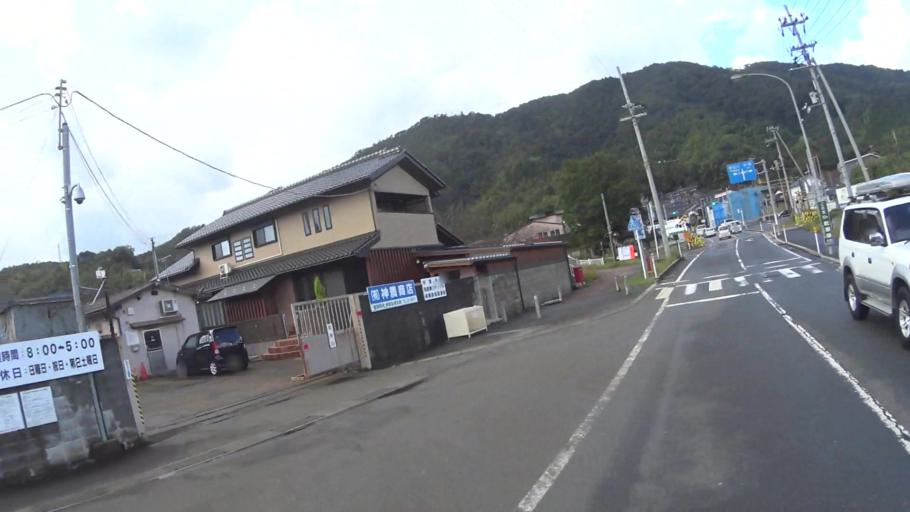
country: JP
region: Kyoto
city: Miyazu
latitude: 35.5531
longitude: 135.1395
